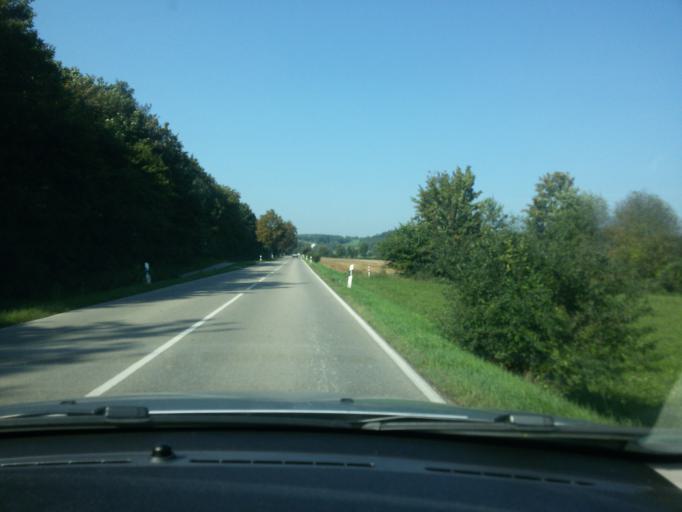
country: DE
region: Bavaria
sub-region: Swabia
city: Hiltenfingen
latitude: 48.1979
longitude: 10.7188
